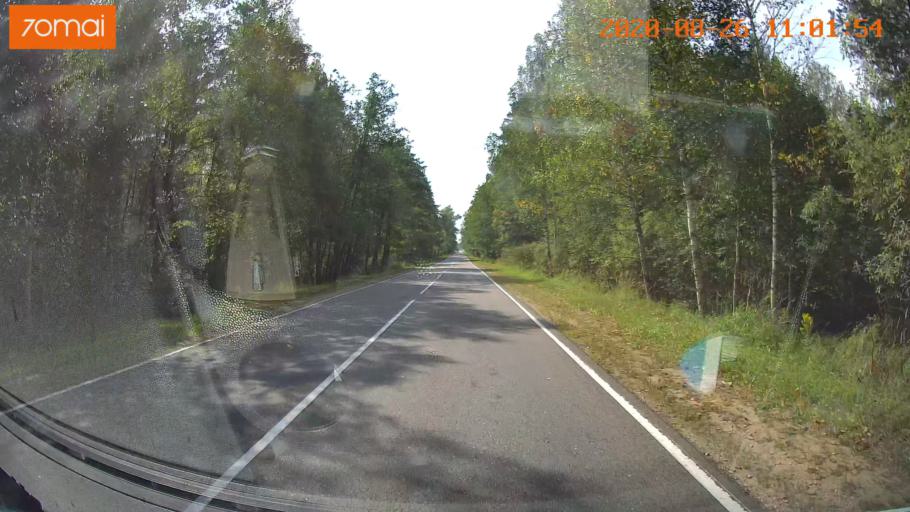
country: RU
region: Rjazan
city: Izhevskoye
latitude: 54.5578
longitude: 41.2271
